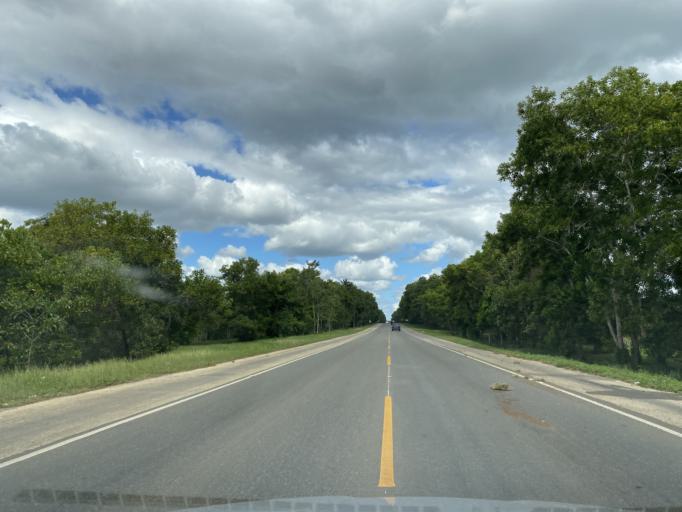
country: DO
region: Santo Domingo
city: Guerra
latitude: 18.6349
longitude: -69.7582
